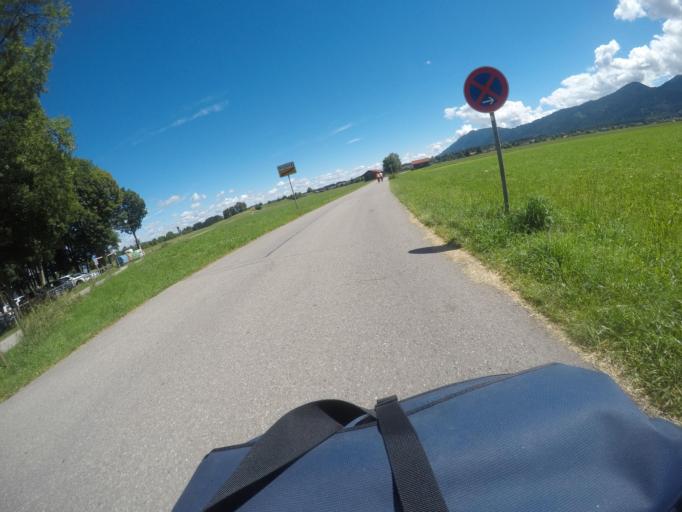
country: DE
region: Bavaria
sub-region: Swabia
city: Schwangau
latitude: 47.5886
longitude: 10.7310
